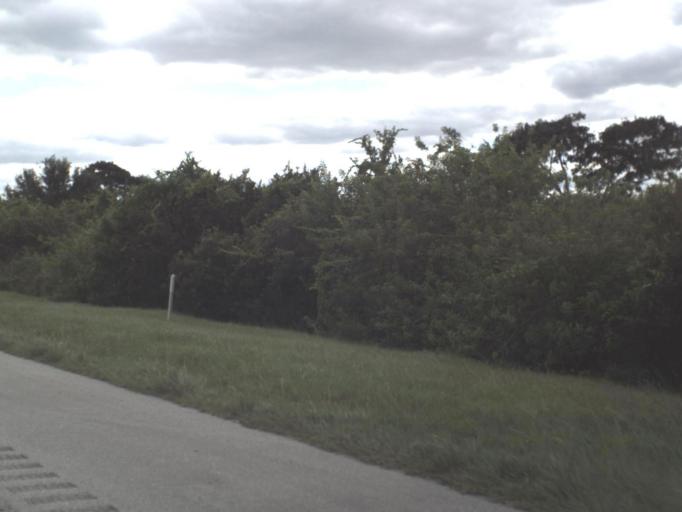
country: US
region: Florida
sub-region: Osceola County
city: Buenaventura Lakes
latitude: 28.2775
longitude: -81.3364
